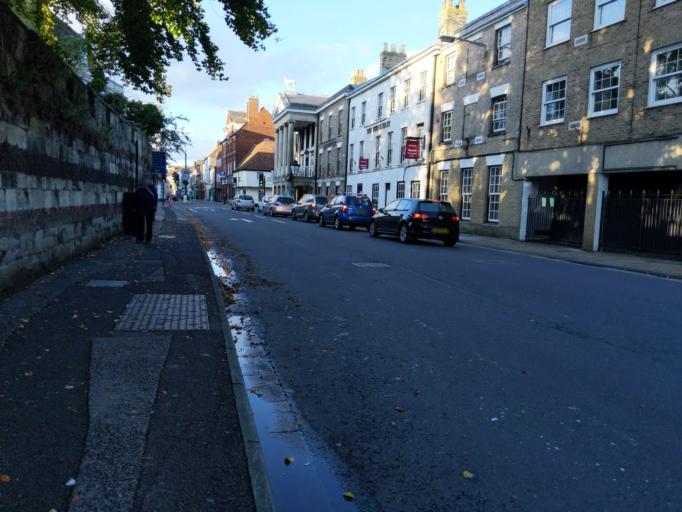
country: GB
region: England
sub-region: Wiltshire
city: Salisbury
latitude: 51.0663
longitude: -1.7936
